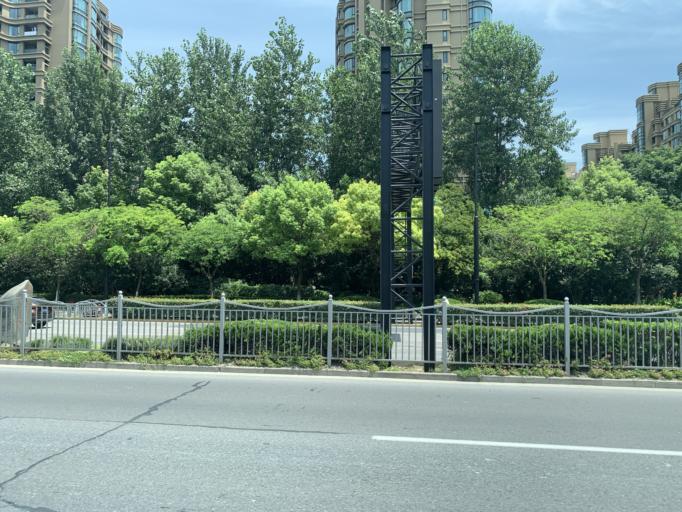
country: CN
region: Shanghai Shi
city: Huamu
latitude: 31.2066
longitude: 121.5260
